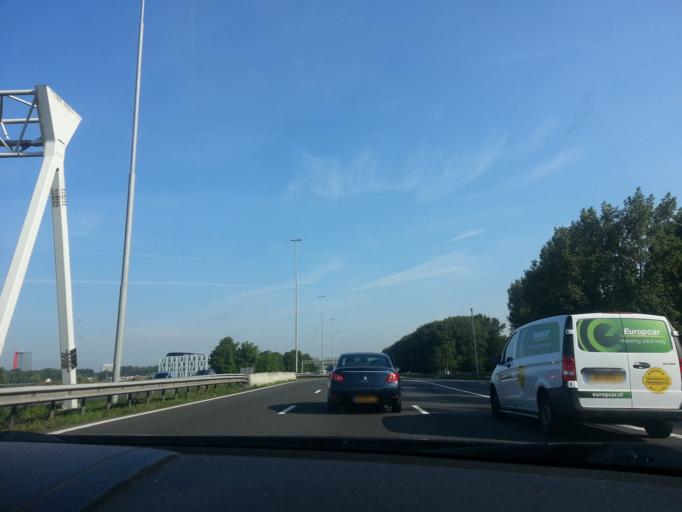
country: NL
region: South Holland
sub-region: Gemeente Delft
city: Delft
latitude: 51.9867
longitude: 4.3933
